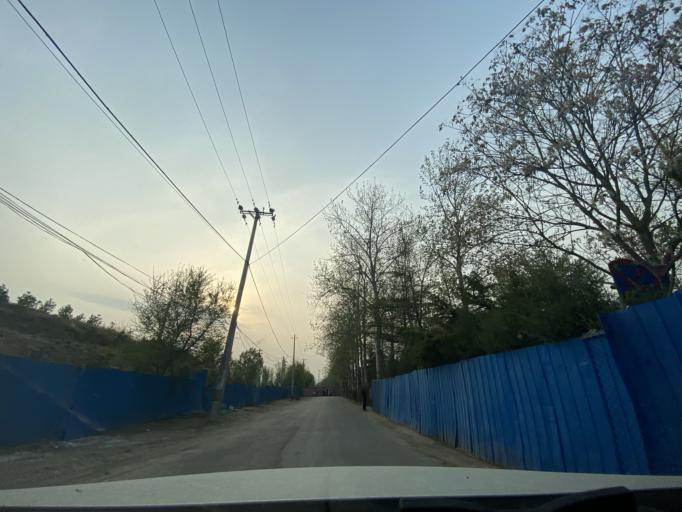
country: CN
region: Beijing
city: Babaoshan
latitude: 39.9327
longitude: 116.2312
